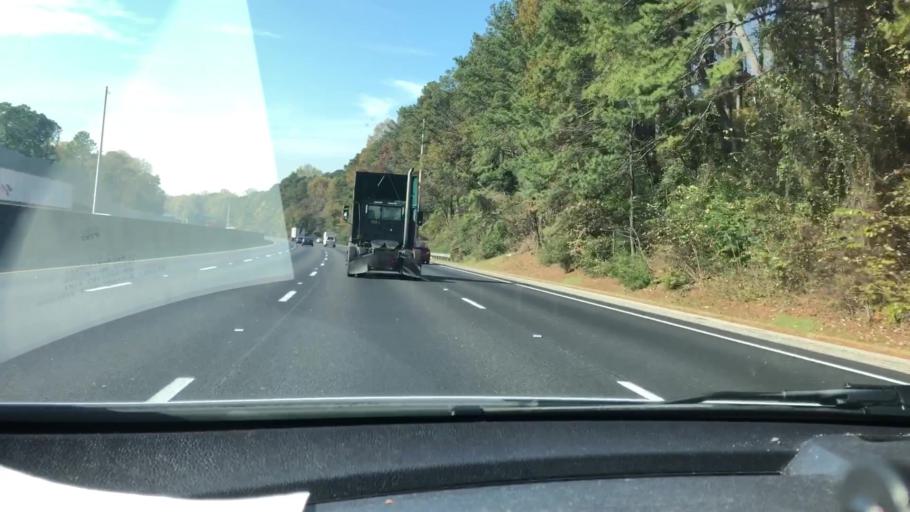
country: US
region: Georgia
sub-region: DeKalb County
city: Panthersville
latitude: 33.6986
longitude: -84.2770
